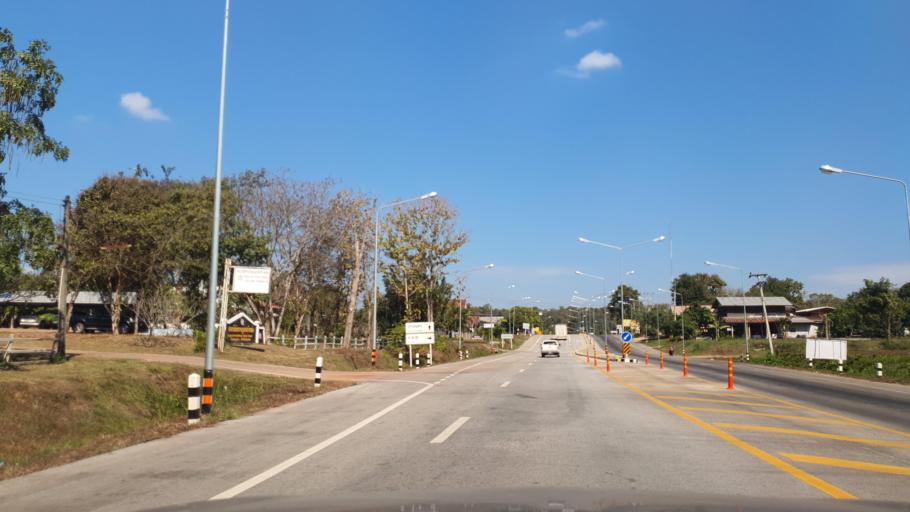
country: TH
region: Kalasin
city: Na Khu
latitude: 16.8557
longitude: 103.9314
